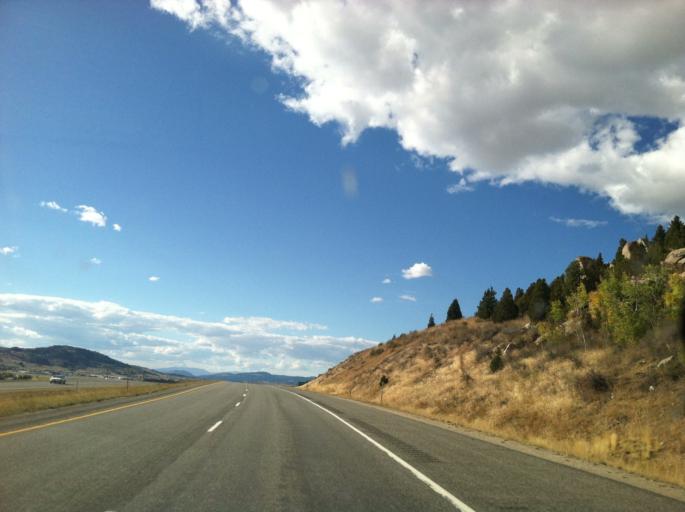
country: US
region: Montana
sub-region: Silver Bow County
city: Butte
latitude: 45.9431
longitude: -112.4610
